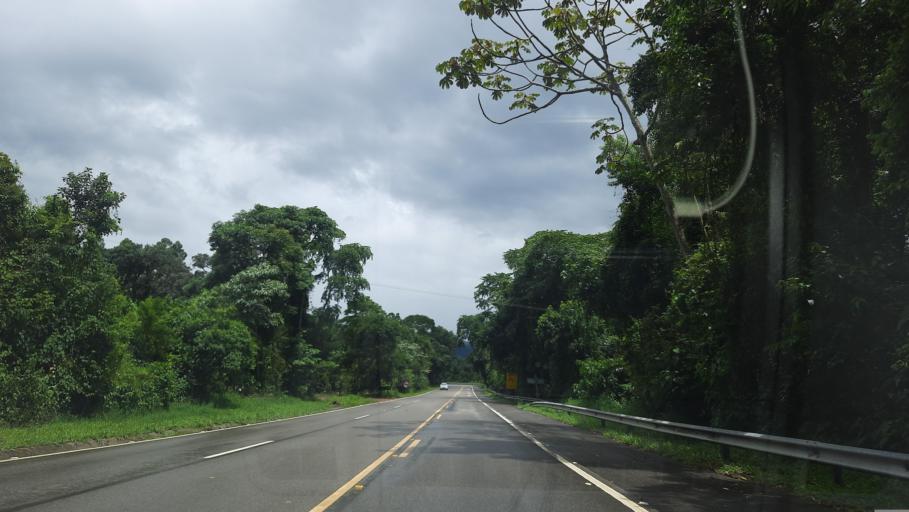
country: BR
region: Minas Gerais
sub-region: Pocos De Caldas
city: Pocos de Caldas
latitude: -21.8444
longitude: -46.6919
